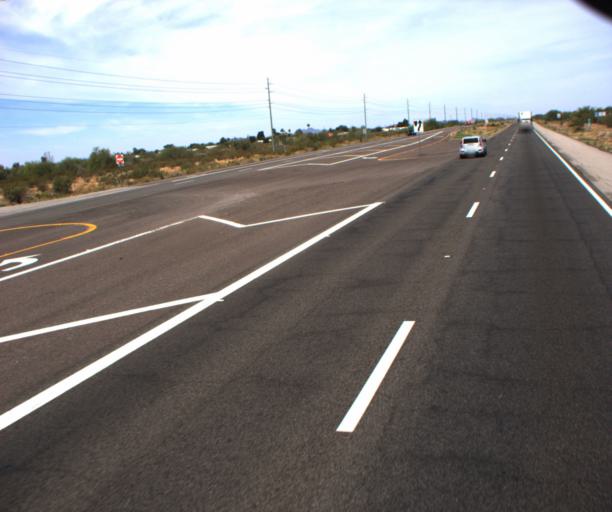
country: US
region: Arizona
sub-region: Maricopa County
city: Sun City West
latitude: 33.7844
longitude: -112.5367
